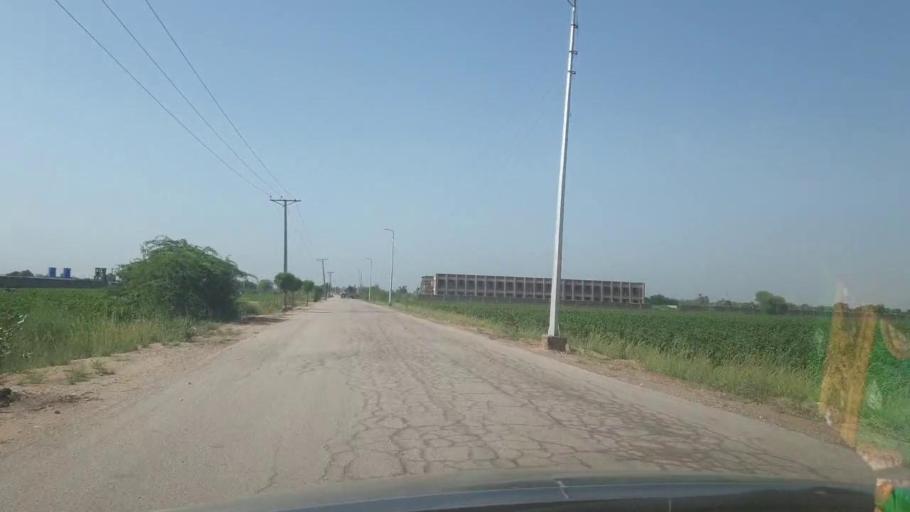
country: PK
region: Sindh
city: Rohri
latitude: 27.5174
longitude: 69.0359
